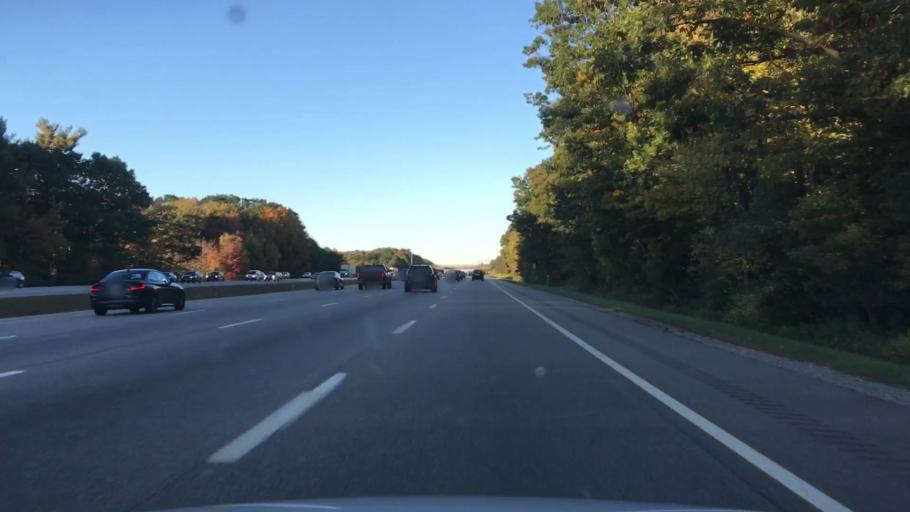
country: US
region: New Hampshire
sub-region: Rockingham County
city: Greenland
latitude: 43.0135
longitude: -70.8348
